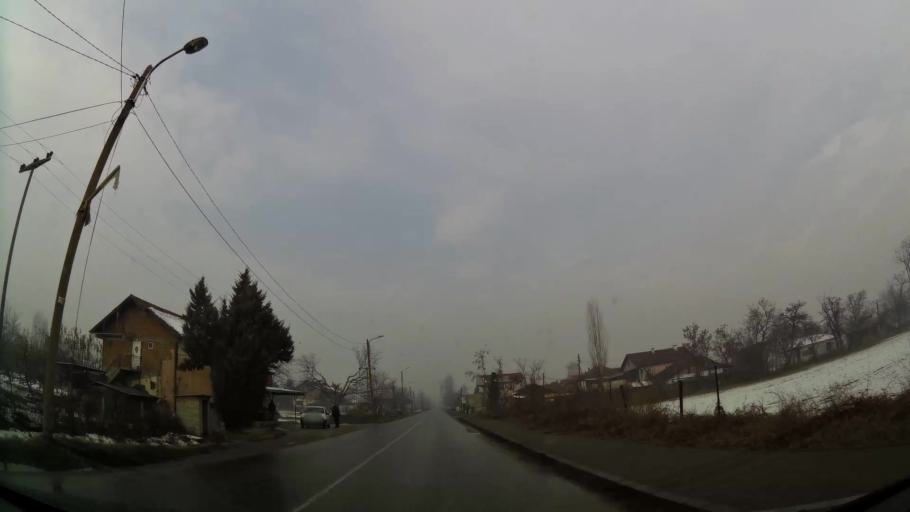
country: MK
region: Ilinden
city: Jurumleri
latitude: 41.9717
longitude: 21.5424
